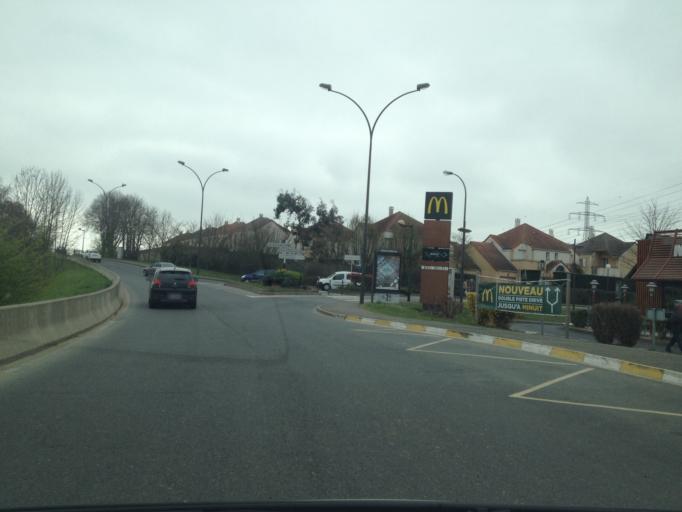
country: FR
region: Ile-de-France
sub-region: Departement de l'Essonne
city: Palaiseau
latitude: 48.7303
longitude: 2.2411
